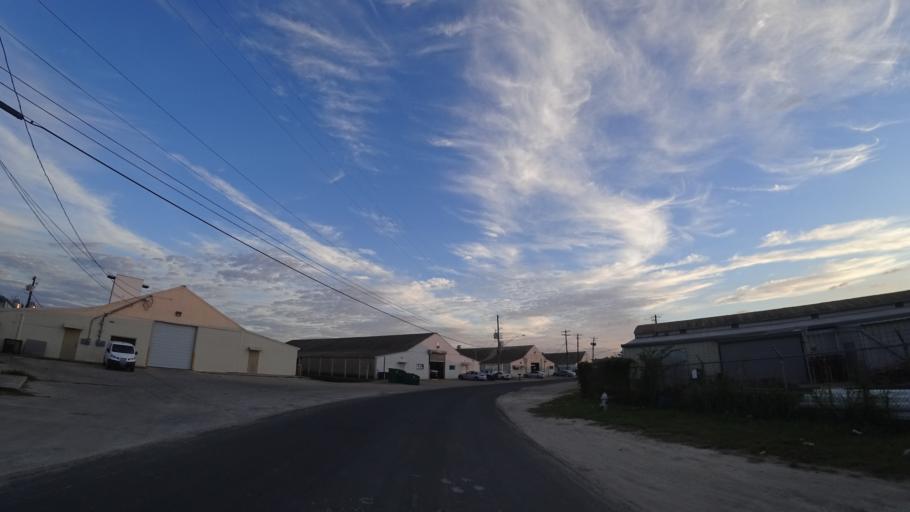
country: US
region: Texas
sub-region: Travis County
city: Austin
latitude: 30.2176
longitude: -97.7623
